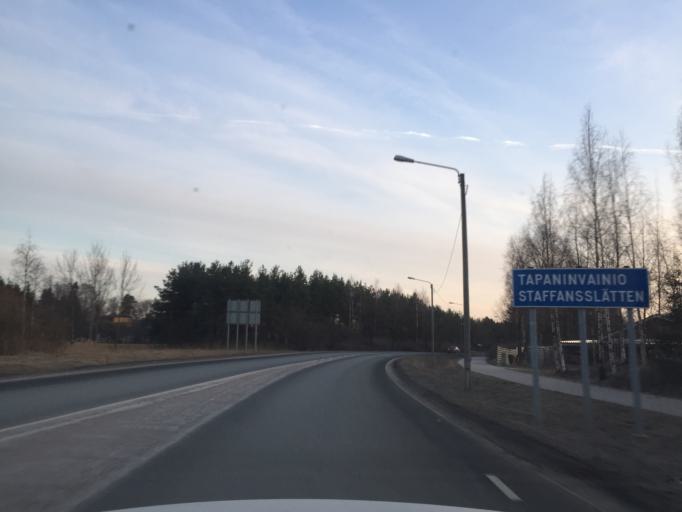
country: FI
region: Uusimaa
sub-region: Helsinki
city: Vantaa
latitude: 60.2632
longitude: 24.9921
